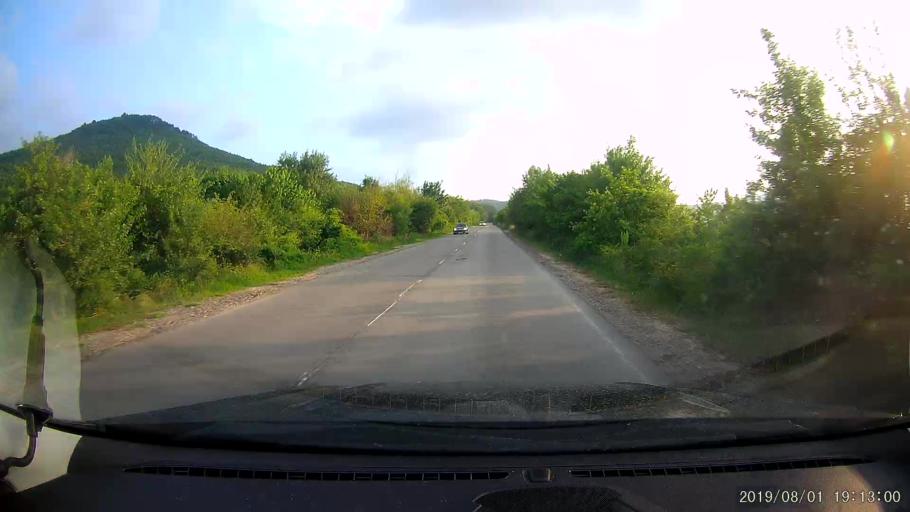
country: BG
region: Shumen
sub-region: Obshtina Smyadovo
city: Smyadovo
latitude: 42.9568
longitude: 26.9452
